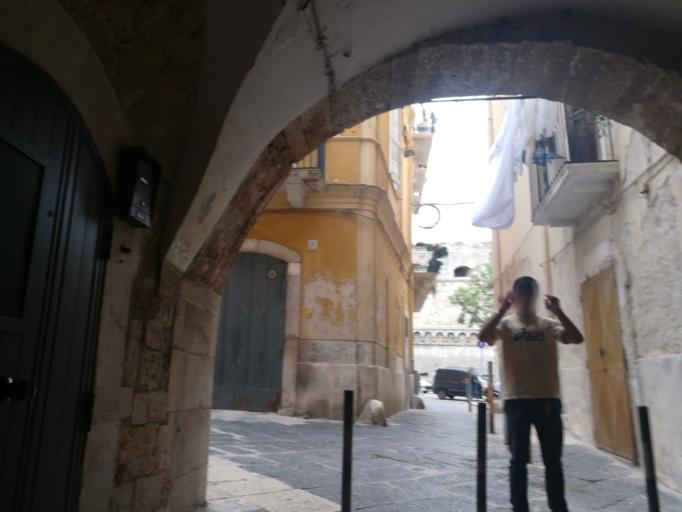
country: IT
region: Apulia
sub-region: Provincia di Bari
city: Bari
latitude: 41.1291
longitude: 16.8679
